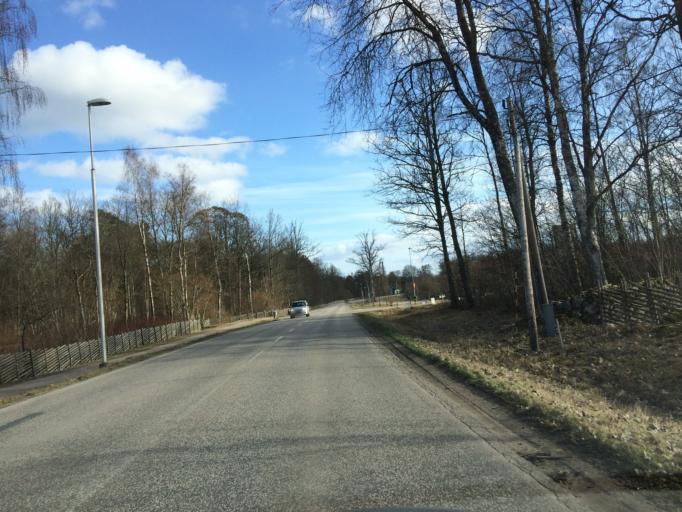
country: SE
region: Kronoberg
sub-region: Almhults Kommun
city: AElmhult
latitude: 56.5655
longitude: 14.1273
